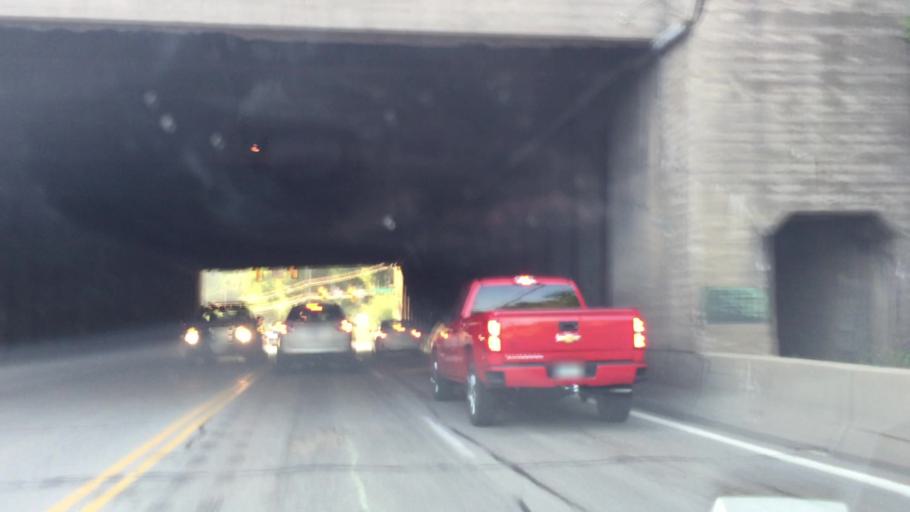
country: US
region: Pennsylvania
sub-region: Allegheny County
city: Pittsburgh
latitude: 40.4253
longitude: -80.0193
